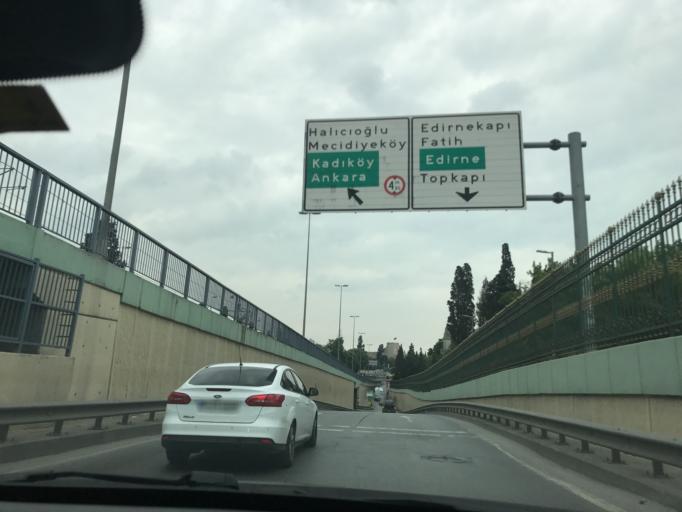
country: TR
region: Istanbul
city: Istanbul
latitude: 41.0335
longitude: 28.9298
